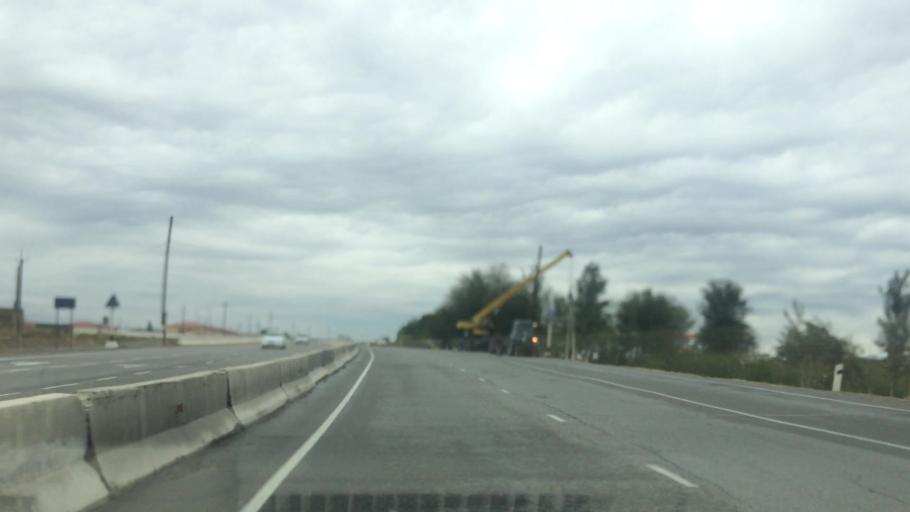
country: UZ
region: Jizzax
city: Jizzax
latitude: 39.9762
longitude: 67.5618
